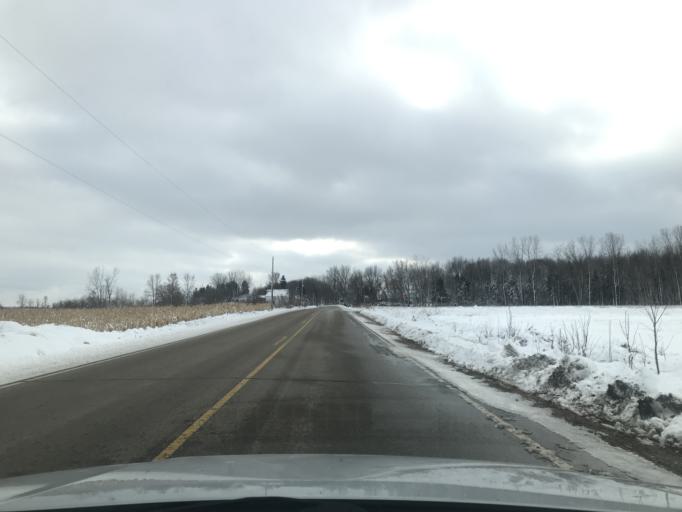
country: US
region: Wisconsin
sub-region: Oconto County
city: Oconto
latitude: 44.9468
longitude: -87.9874
